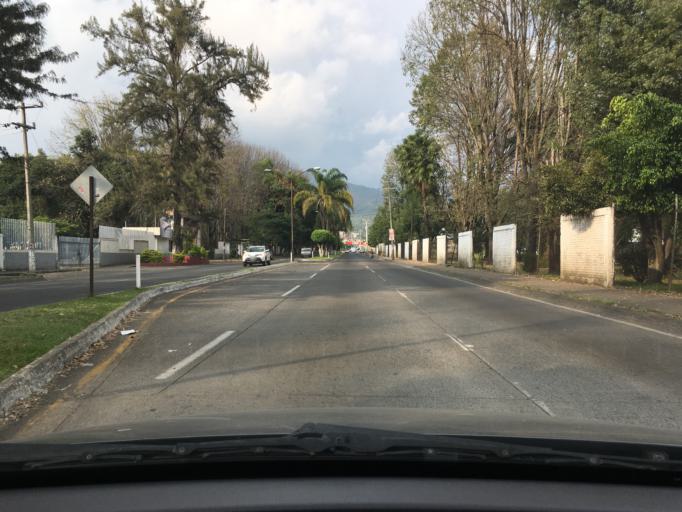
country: MX
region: Michoacan
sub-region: Uruapan
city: Uruapan
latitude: 19.4145
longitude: -102.0468
